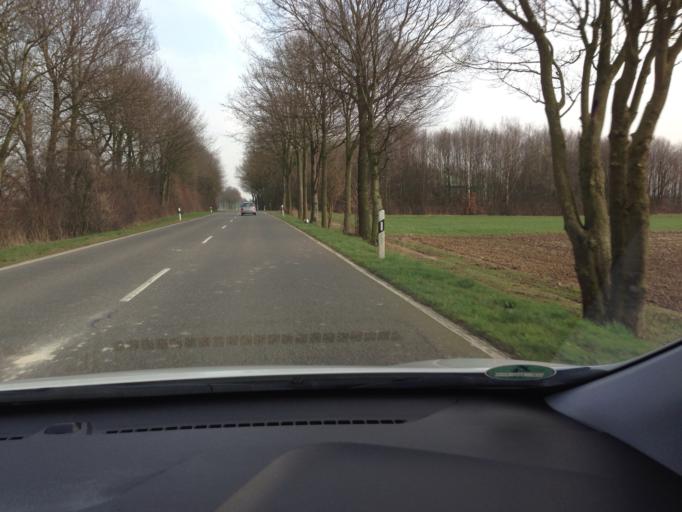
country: DE
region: North Rhine-Westphalia
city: Huckelhoven
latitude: 51.0824
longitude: 6.2643
